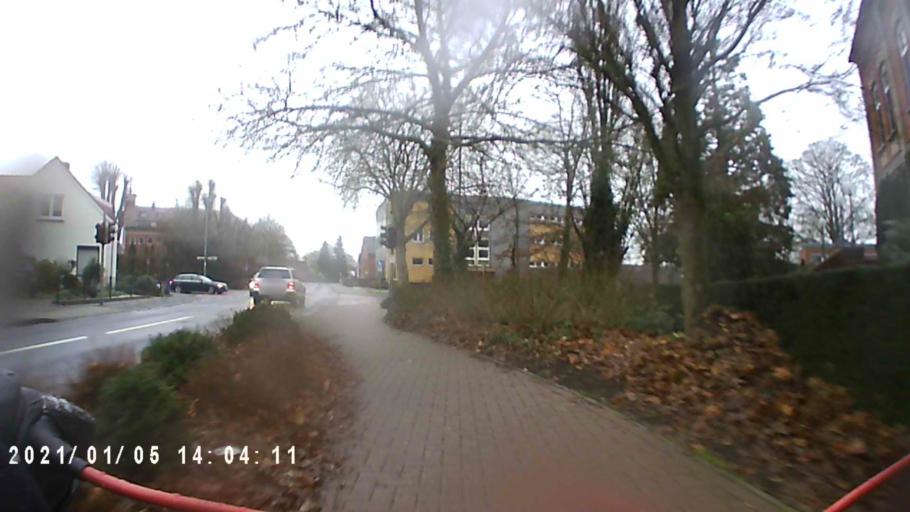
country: DE
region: Lower Saxony
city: Weener
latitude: 53.1643
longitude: 7.3469
